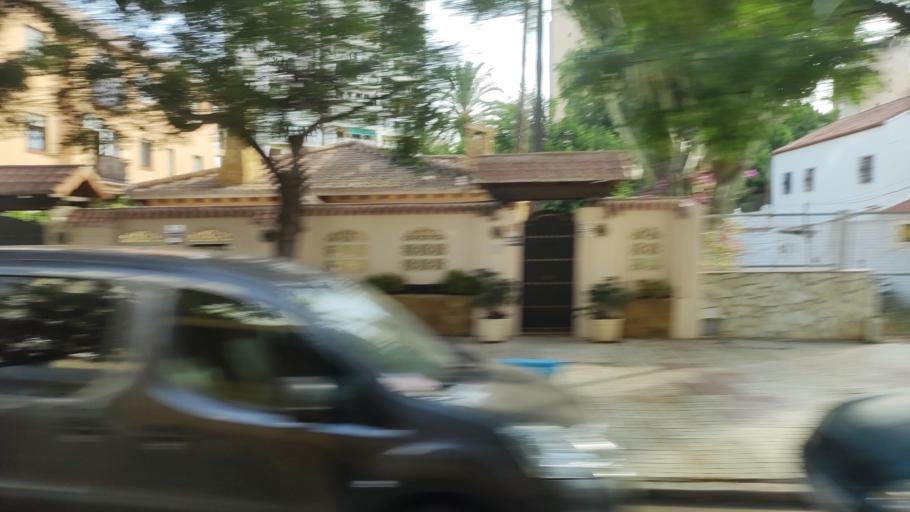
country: ES
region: Andalusia
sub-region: Provincia de Malaga
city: Torremolinos
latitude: 36.6276
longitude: -4.4942
